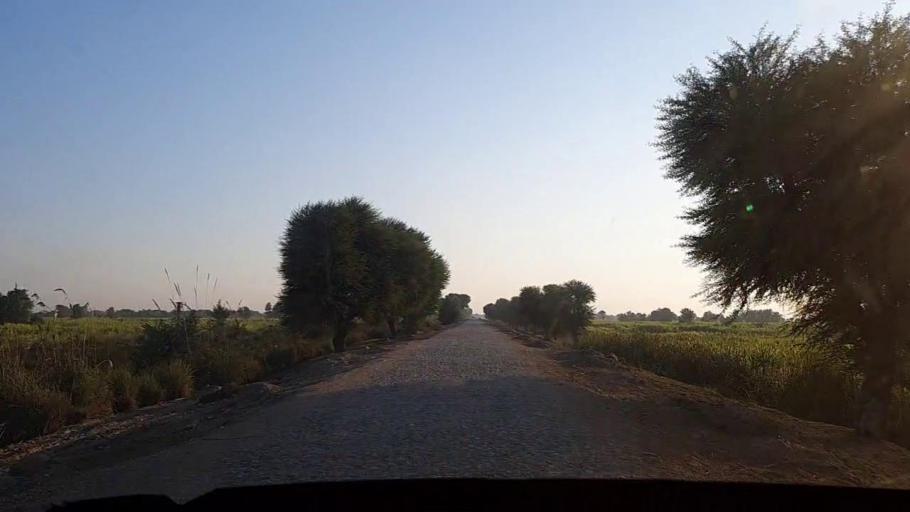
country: PK
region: Sindh
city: Sobhadero
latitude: 27.3765
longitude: 68.3796
